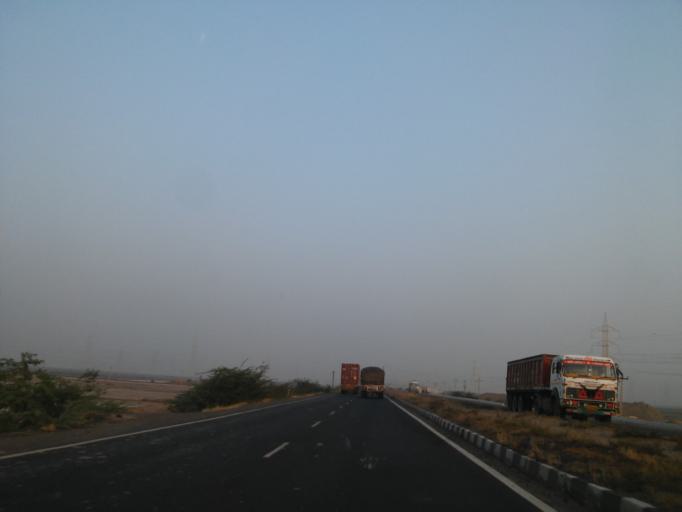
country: IN
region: Gujarat
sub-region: Rajkot
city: Morbi
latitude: 23.1380
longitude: 70.7501
